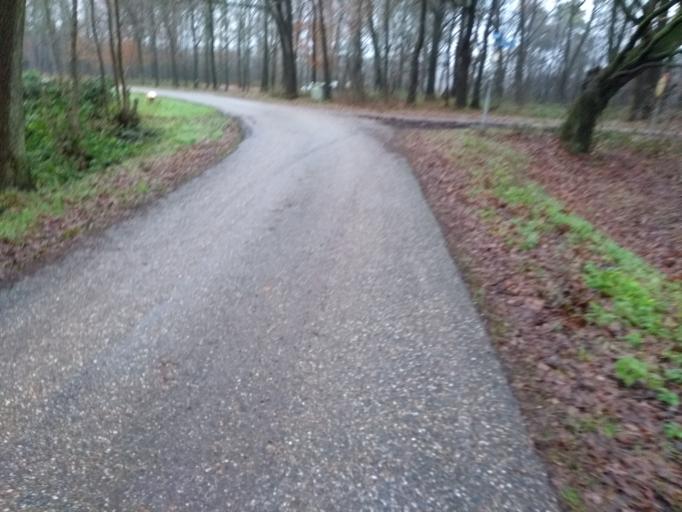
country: NL
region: Overijssel
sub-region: Gemeente Haaksbergen
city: Haaksbergen
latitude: 52.1244
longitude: 6.7618
